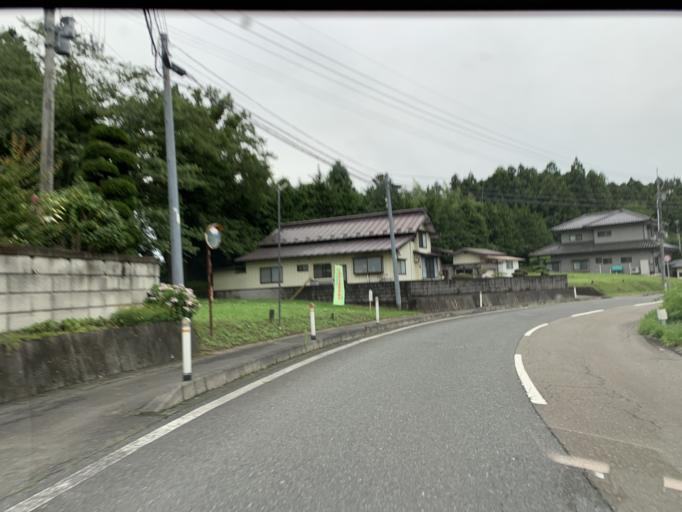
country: JP
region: Iwate
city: Ichinoseki
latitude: 38.8120
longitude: 141.1966
